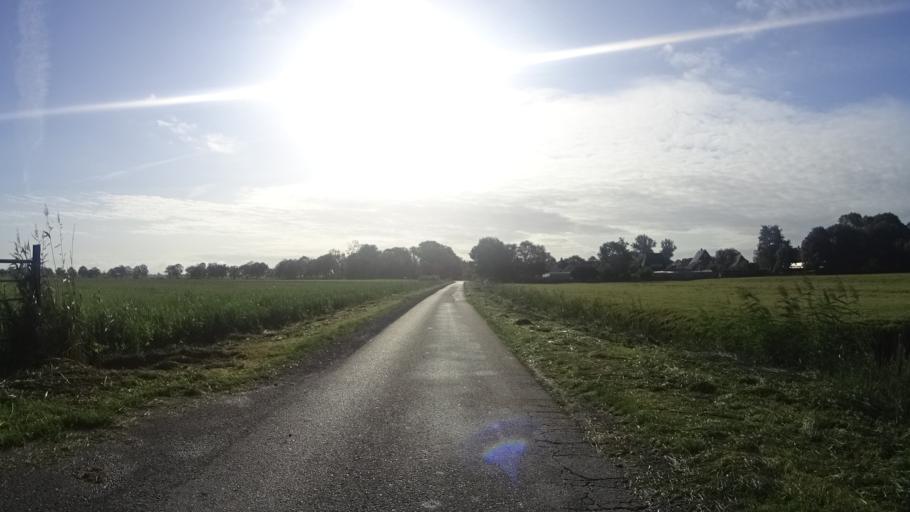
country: DE
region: Lower Saxony
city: Nordenham
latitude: 53.4955
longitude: 8.4402
